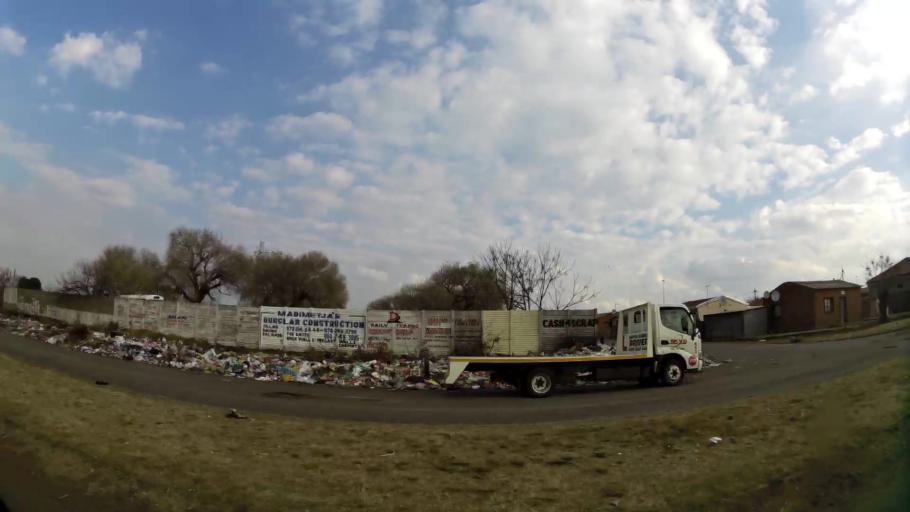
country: ZA
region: Gauteng
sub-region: Sedibeng District Municipality
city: Vanderbijlpark
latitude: -26.6902
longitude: 27.8773
